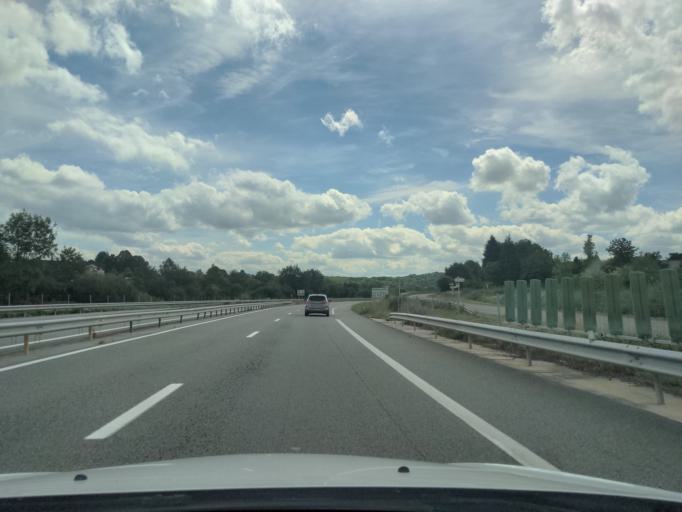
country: FR
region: Limousin
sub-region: Departement de la Creuse
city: Saint-Vaury
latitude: 46.2105
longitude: 1.7420
